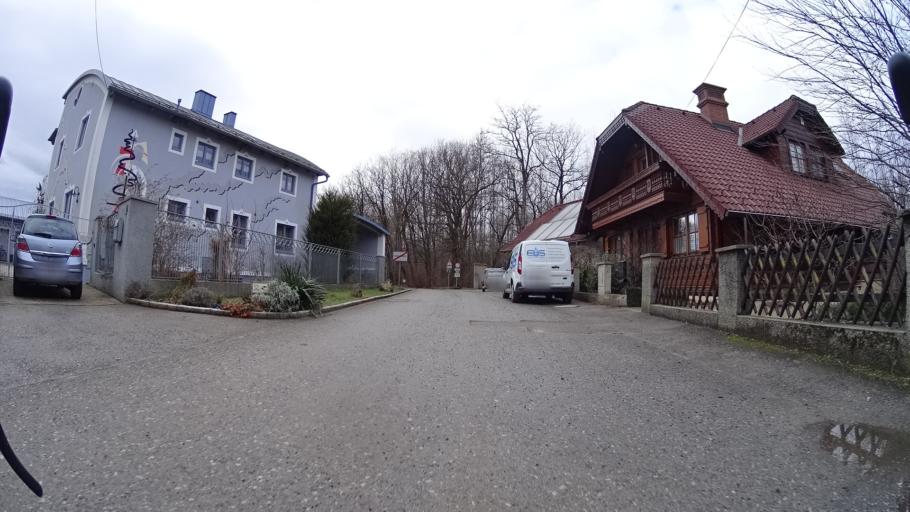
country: AT
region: Lower Austria
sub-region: Politischer Bezirk Tulln
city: Langenrohr
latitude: 48.3314
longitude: 15.9732
